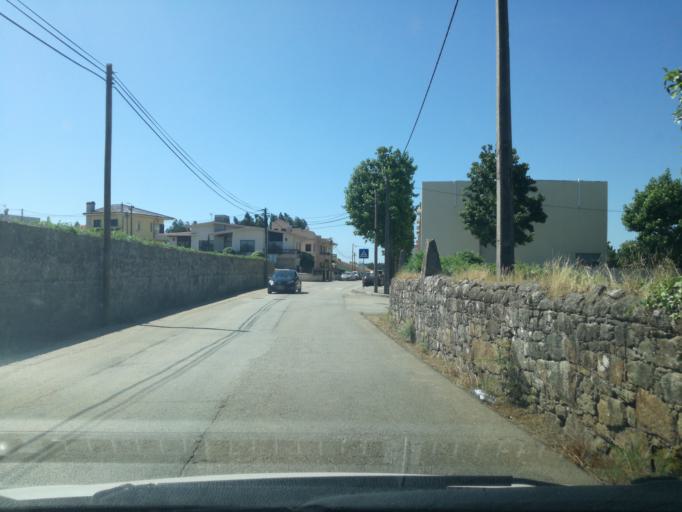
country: PT
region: Porto
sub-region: Maia
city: Gemunde
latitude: 41.2702
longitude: -8.6369
